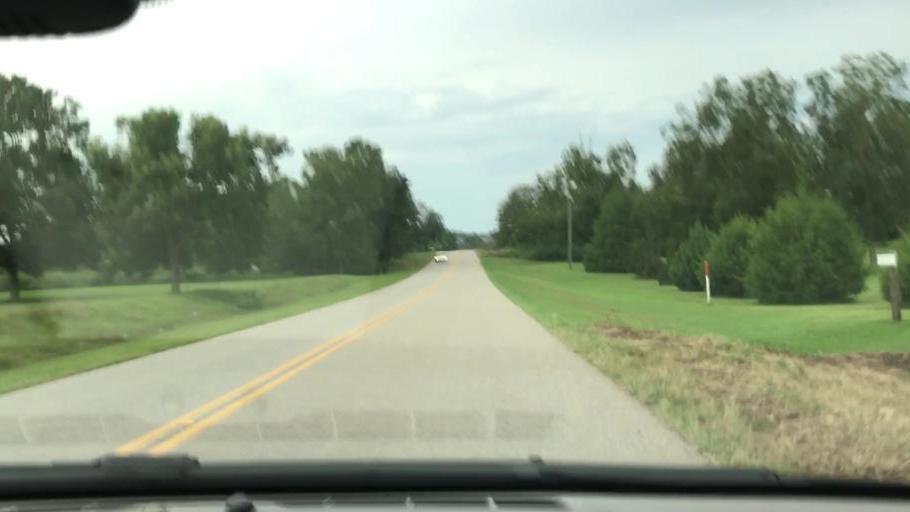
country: US
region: Alabama
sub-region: Houston County
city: Ashford
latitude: 31.2517
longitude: -85.1673
